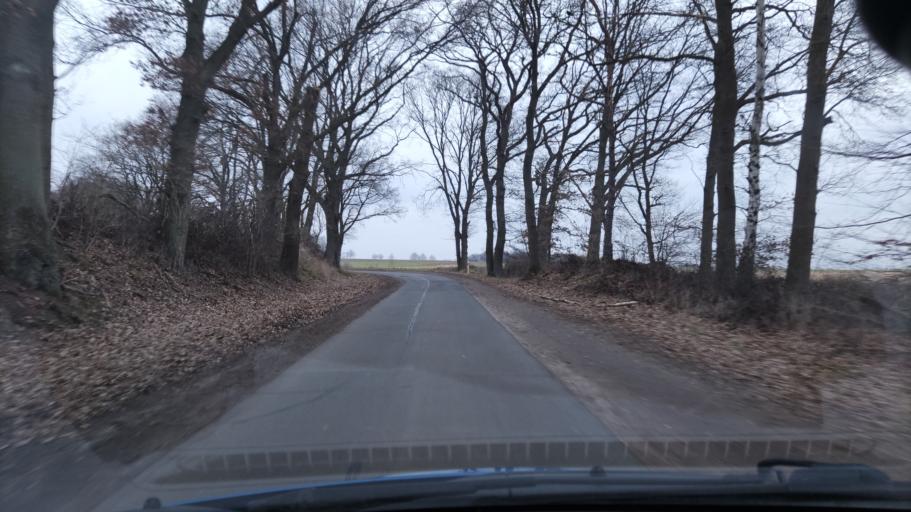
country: DE
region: Lower Saxony
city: Melbeck
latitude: 53.1778
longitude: 10.3876
